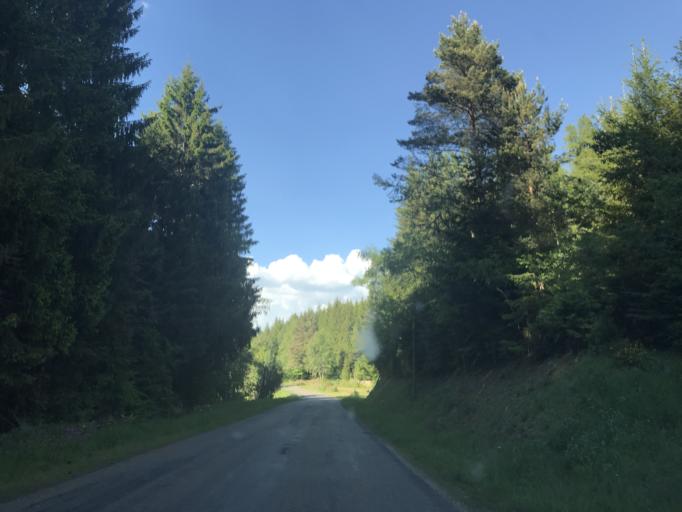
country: FR
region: Auvergne
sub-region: Departement du Puy-de-Dome
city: Cunlhat
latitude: 45.6002
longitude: 3.6505
